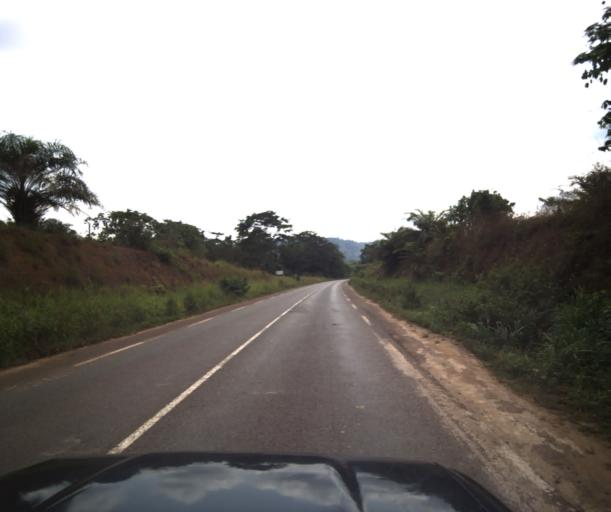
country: CM
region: Centre
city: Eseka
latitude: 3.8919
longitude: 10.7170
